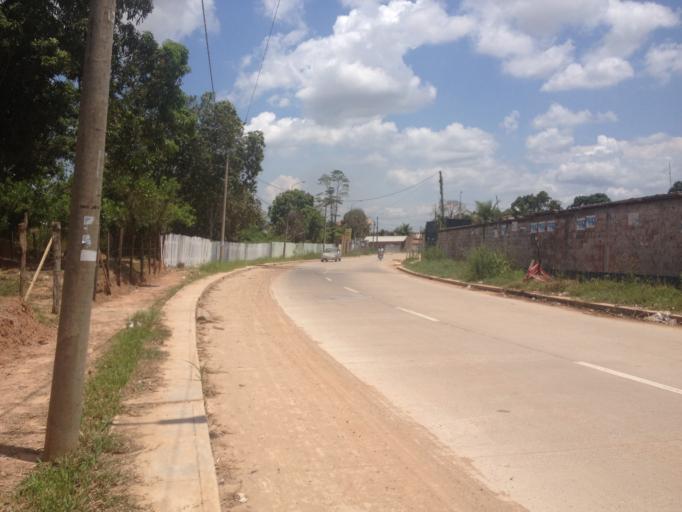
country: PE
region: Ucayali
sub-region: Provincia de Coronel Portillo
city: Pucallpa
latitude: -8.3783
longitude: -74.5606
